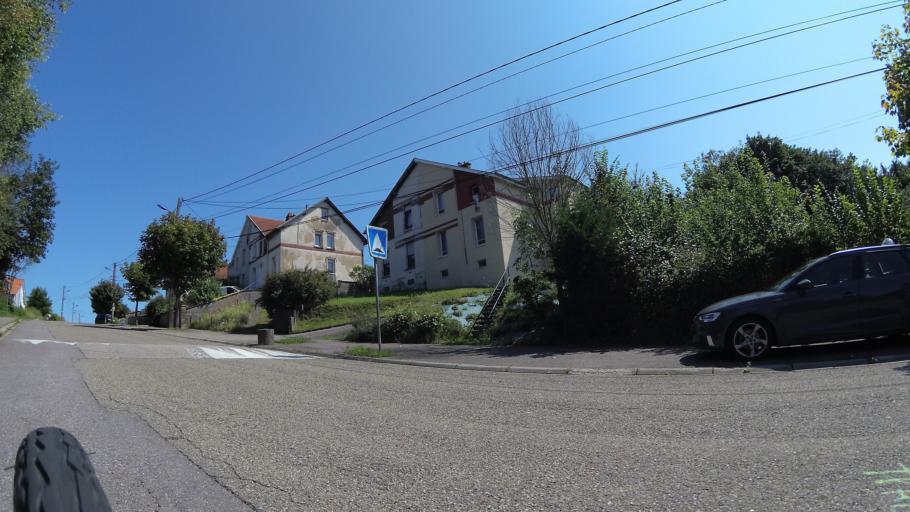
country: FR
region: Lorraine
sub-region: Departement de la Moselle
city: Stiring-Wendel
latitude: 49.2070
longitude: 6.9402
